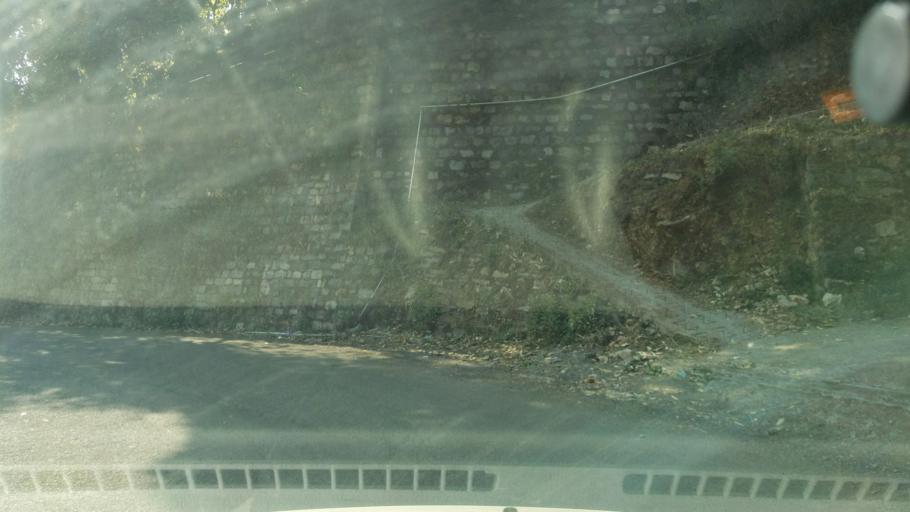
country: IN
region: Uttarakhand
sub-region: Naini Tal
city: Bhowali
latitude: 29.3924
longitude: 79.5330
